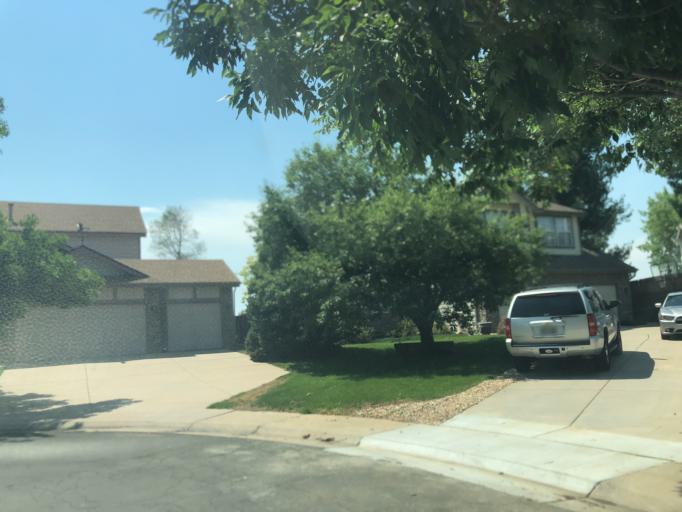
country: US
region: Colorado
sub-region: Arapahoe County
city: Dove Valley
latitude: 39.6362
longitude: -104.7720
